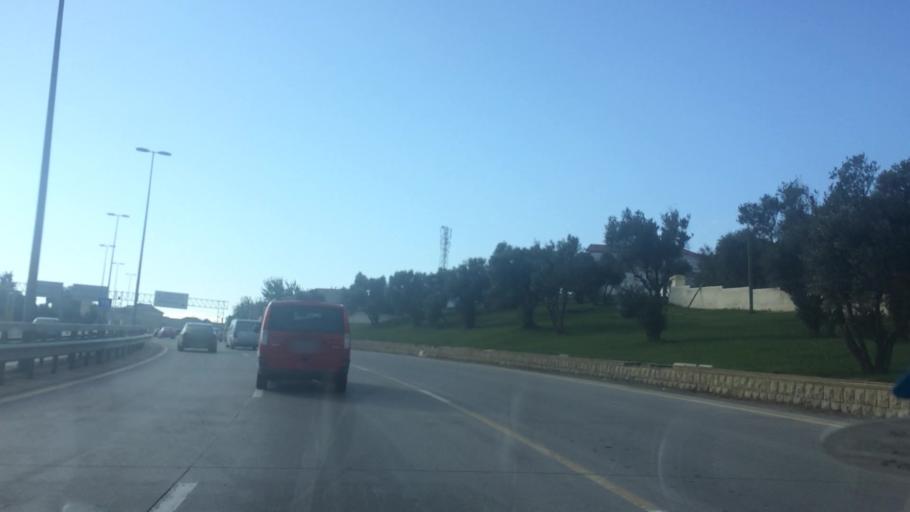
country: AZ
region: Baki
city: Qaracuxur
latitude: 40.3487
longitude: 49.9647
